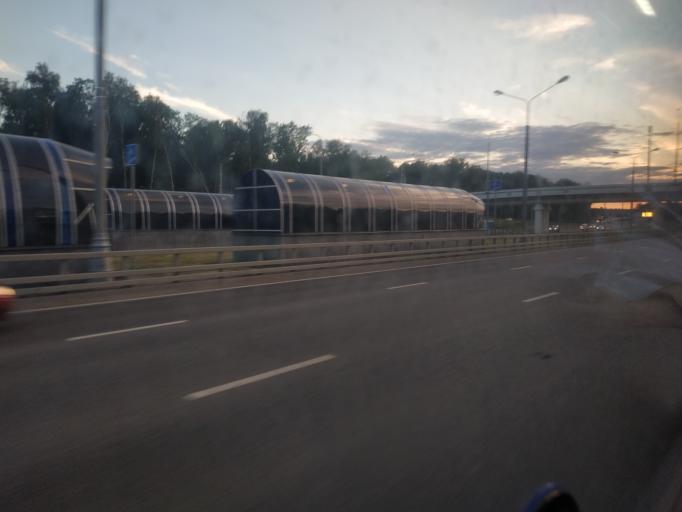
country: RU
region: Moscow
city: Solntsevo
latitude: 55.6084
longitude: 37.3951
